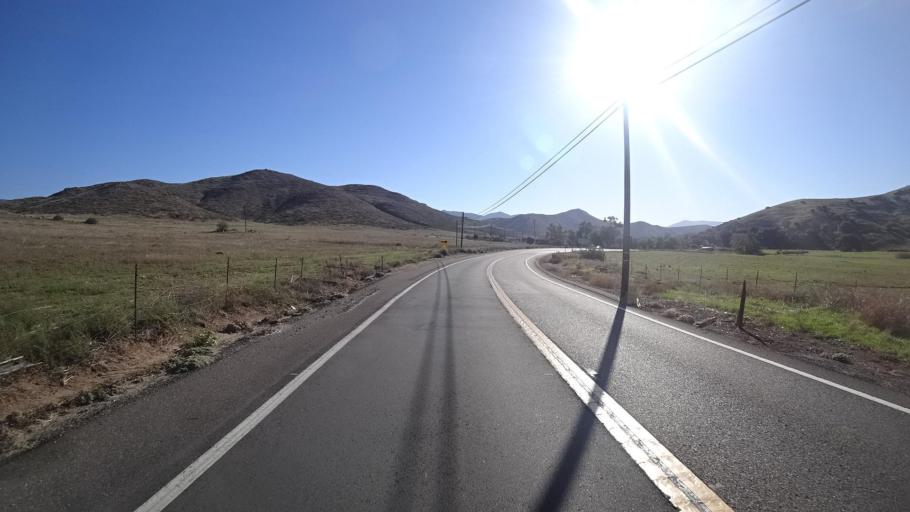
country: US
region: California
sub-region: San Diego County
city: Jamul
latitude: 32.6705
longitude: -116.8269
